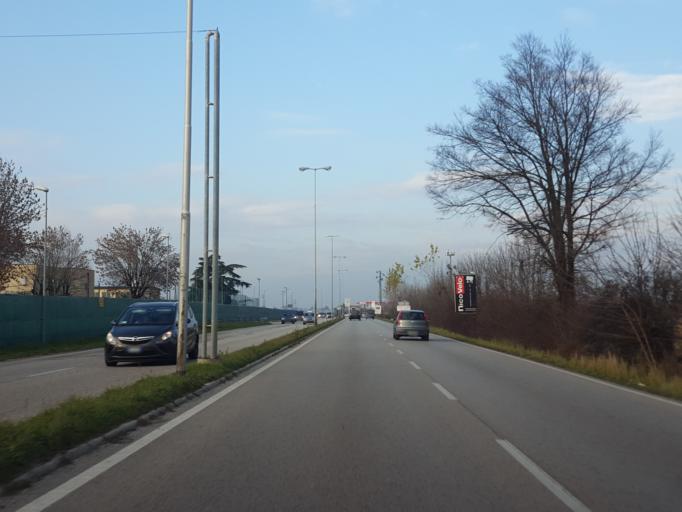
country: IT
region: Veneto
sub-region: Provincia di Vicenza
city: Villaggio Montegrappa
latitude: 45.5474
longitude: 11.5847
